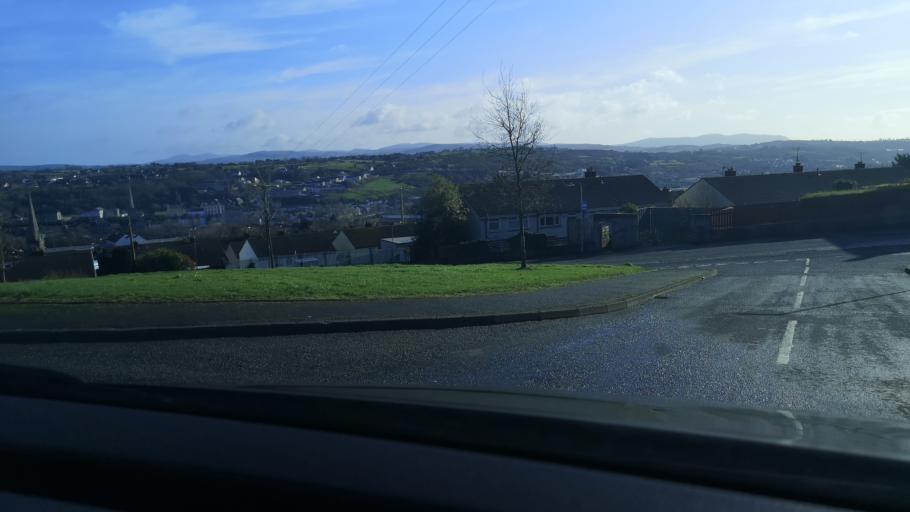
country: GB
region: Northern Ireland
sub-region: Newry and Mourne District
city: Newry
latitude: 54.1714
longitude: -6.3498
